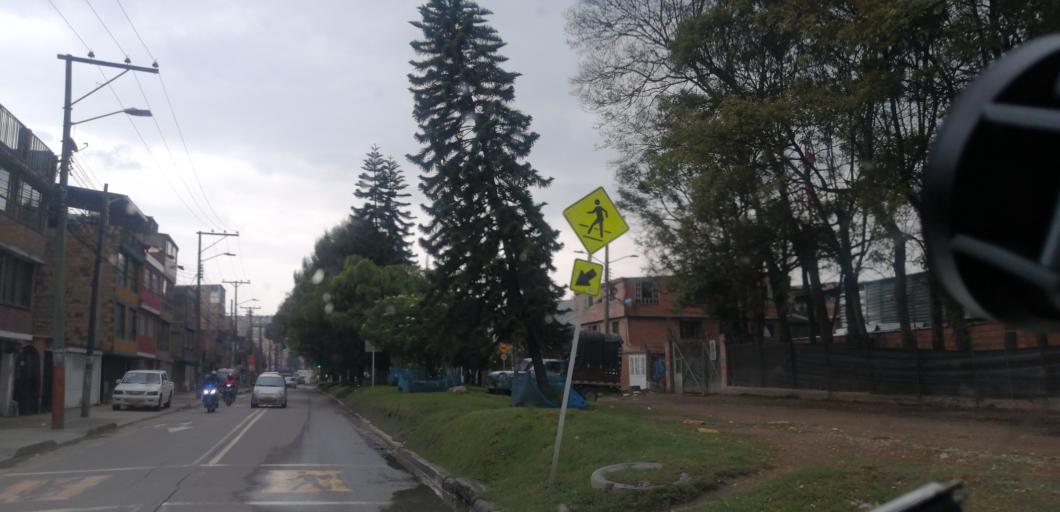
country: CO
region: Cundinamarca
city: Funza
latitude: 4.6855
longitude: -74.1525
